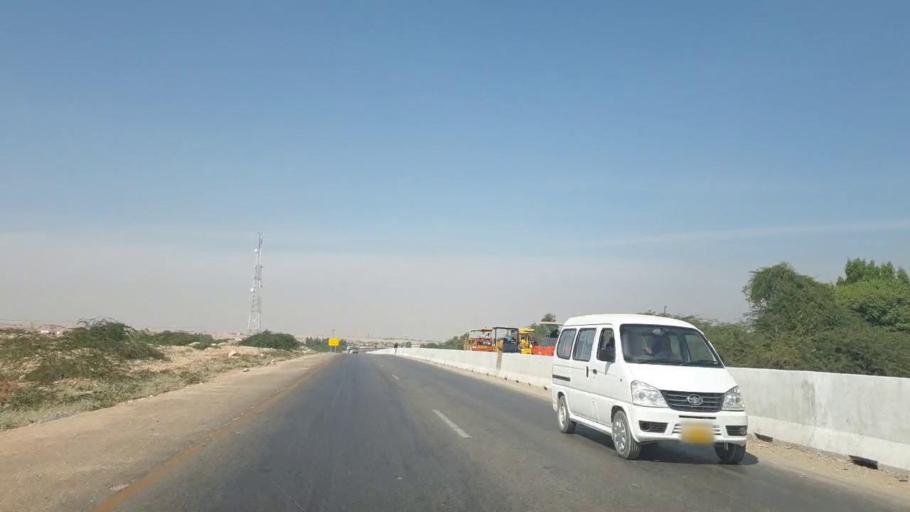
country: PK
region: Sindh
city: Hala
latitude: 25.7157
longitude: 68.2950
